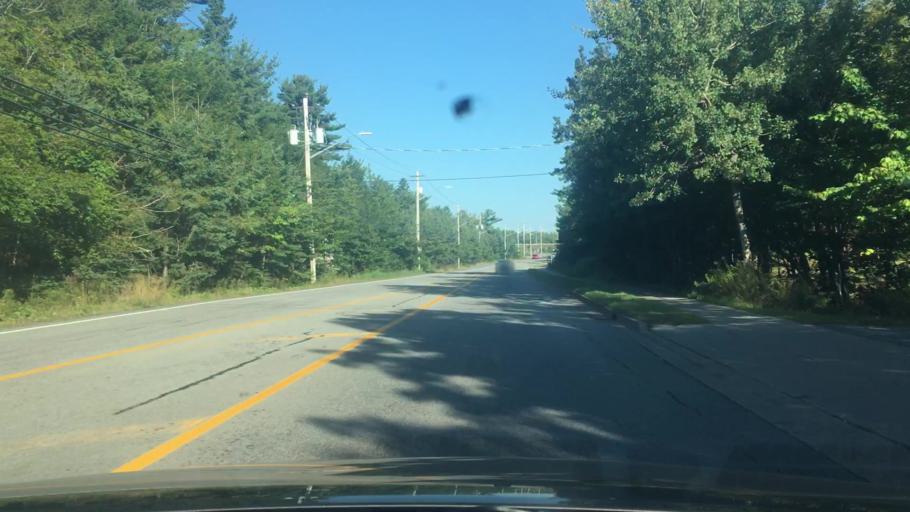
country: CA
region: Nova Scotia
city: Dartmouth
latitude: 44.7191
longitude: -63.6859
